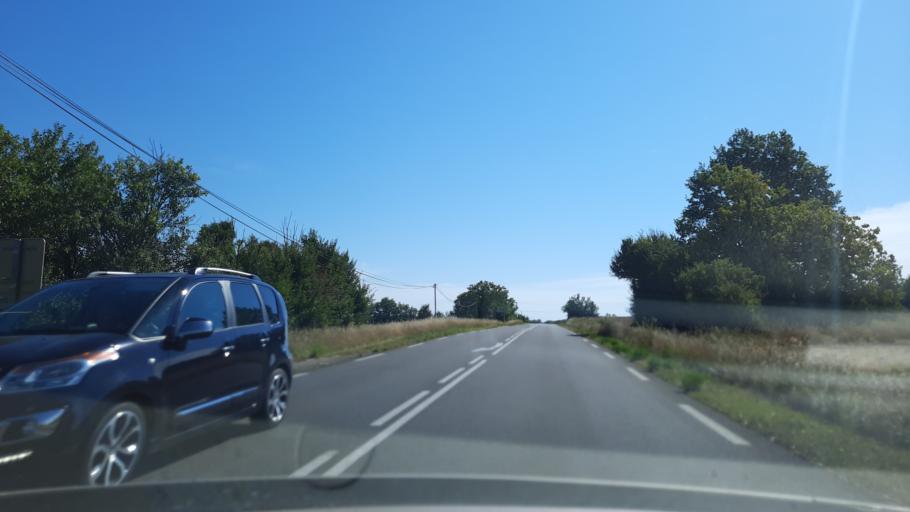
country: FR
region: Midi-Pyrenees
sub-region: Departement du Tarn-et-Garonne
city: Septfonds
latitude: 44.1926
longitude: 1.6776
